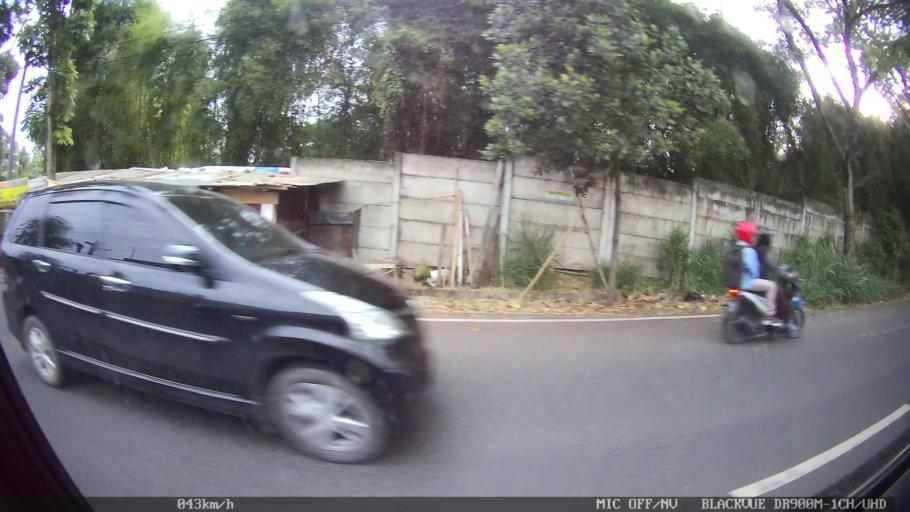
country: ID
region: Lampung
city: Bandarlampung
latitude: -5.4327
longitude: 105.2429
